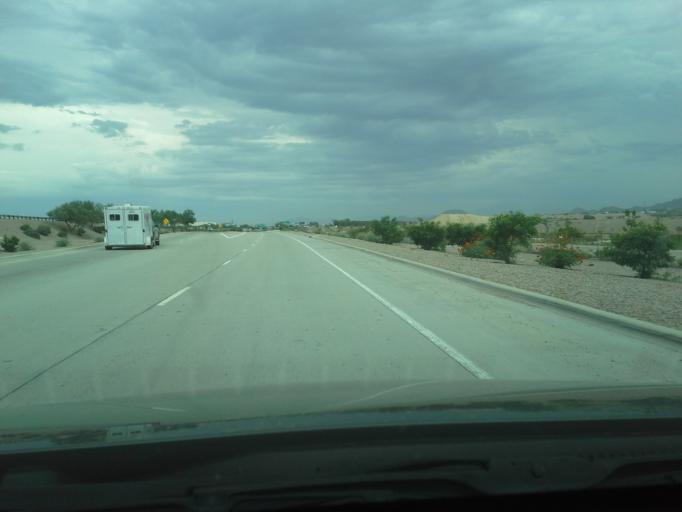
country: US
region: Arizona
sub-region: Pima County
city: Flowing Wells
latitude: 32.3224
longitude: -111.0520
